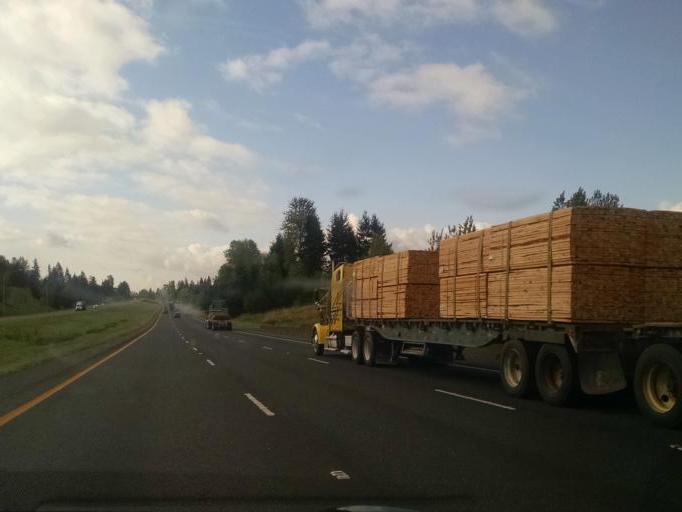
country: US
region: Washington
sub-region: Cowlitz County
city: Kelso
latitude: 46.1647
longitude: -122.9037
